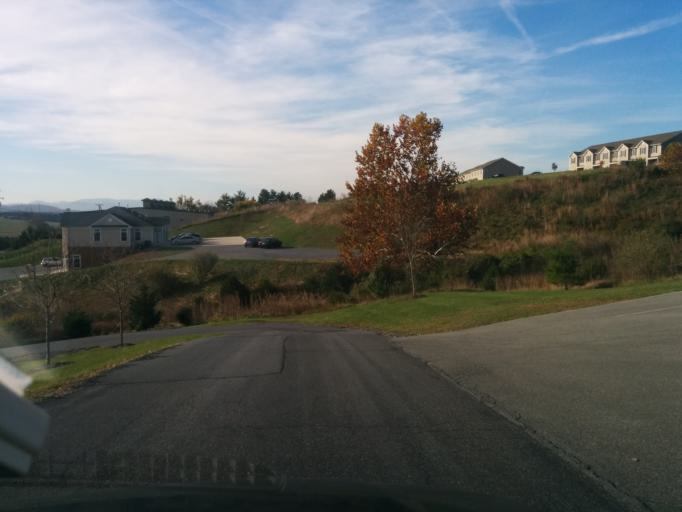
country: US
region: Virginia
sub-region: Rockbridge County
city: East Lexington
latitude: 37.8109
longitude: -79.4002
